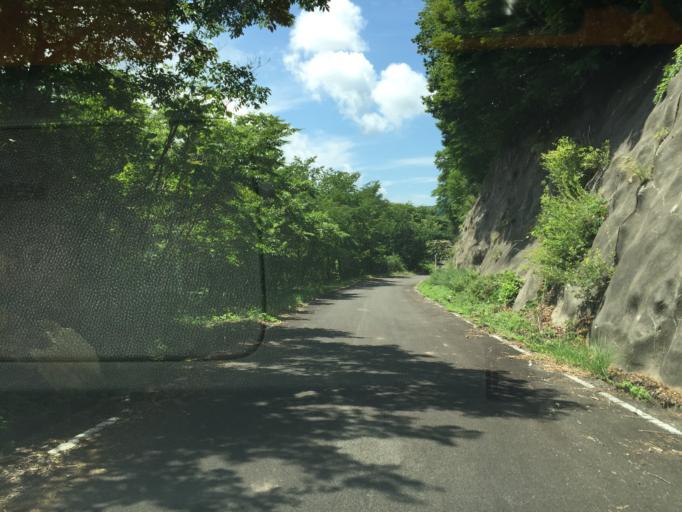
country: JP
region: Fukushima
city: Inawashiro
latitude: 37.4460
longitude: 140.0538
